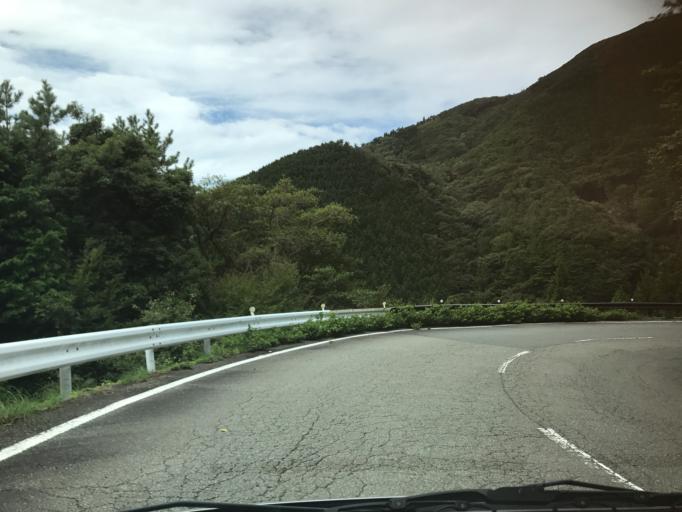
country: JP
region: Shizuoka
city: Heda
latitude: 34.9771
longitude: 138.8249
